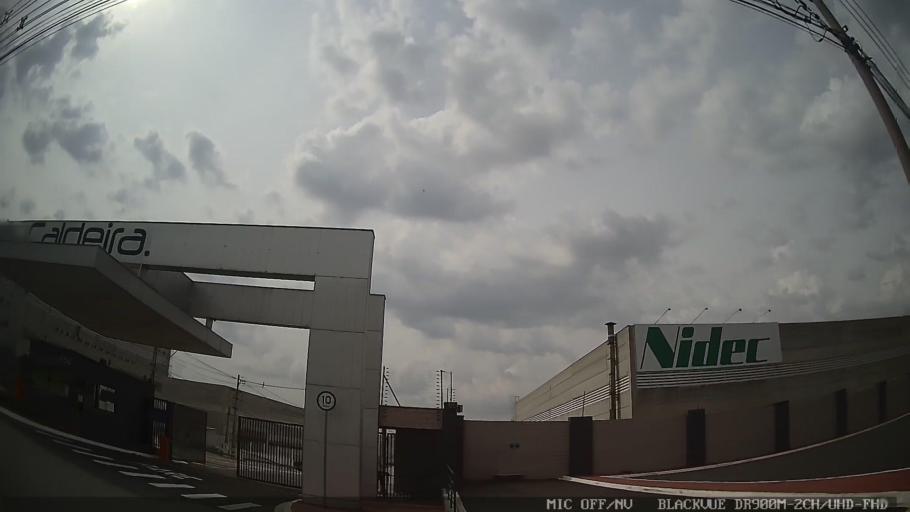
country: BR
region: Sao Paulo
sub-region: Indaiatuba
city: Indaiatuba
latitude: -23.1326
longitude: -47.2495
